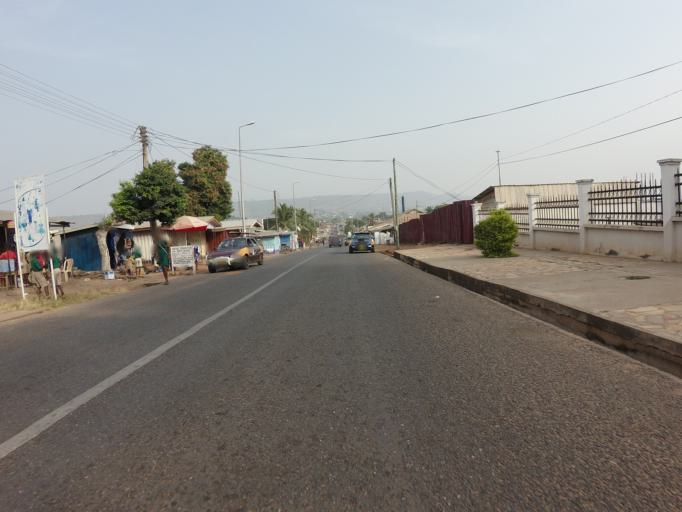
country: GH
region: Volta
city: Ho
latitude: 6.6038
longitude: 0.4751
